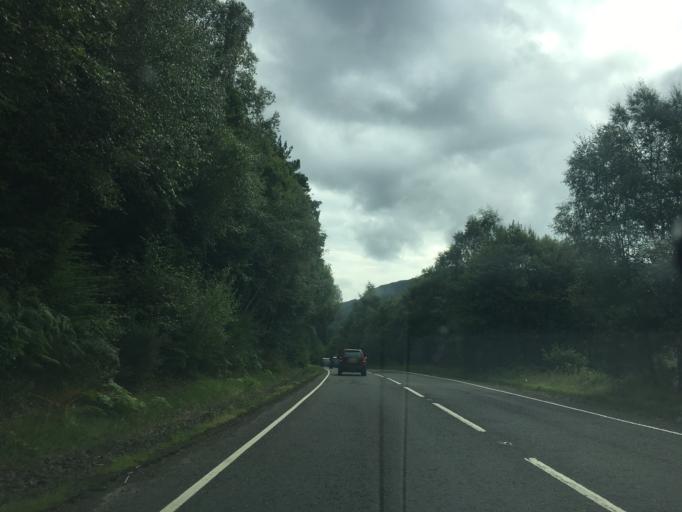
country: GB
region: Scotland
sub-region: Stirling
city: Callander
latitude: 56.3121
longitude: -4.3270
